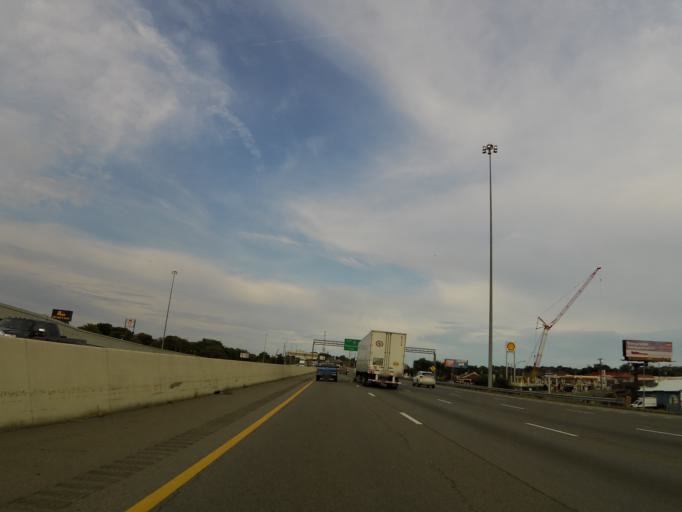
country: US
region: Tennessee
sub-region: Davidson County
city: Belle Meade
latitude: 36.1537
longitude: -86.8447
